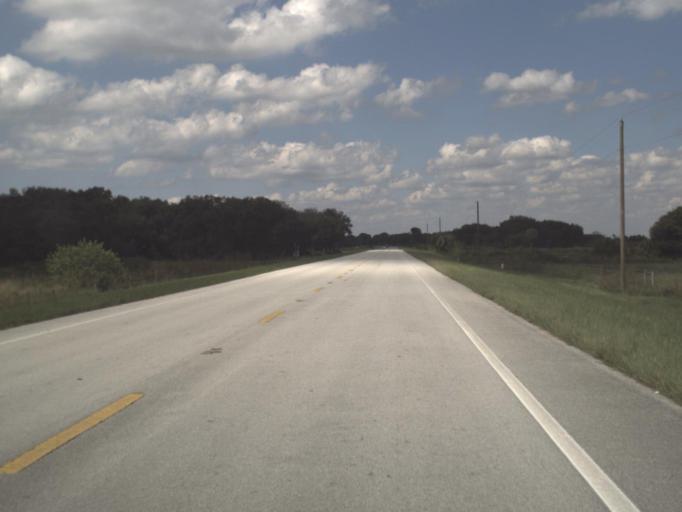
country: US
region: Florida
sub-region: Highlands County
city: Lake Placid
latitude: 27.3778
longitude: -81.0992
